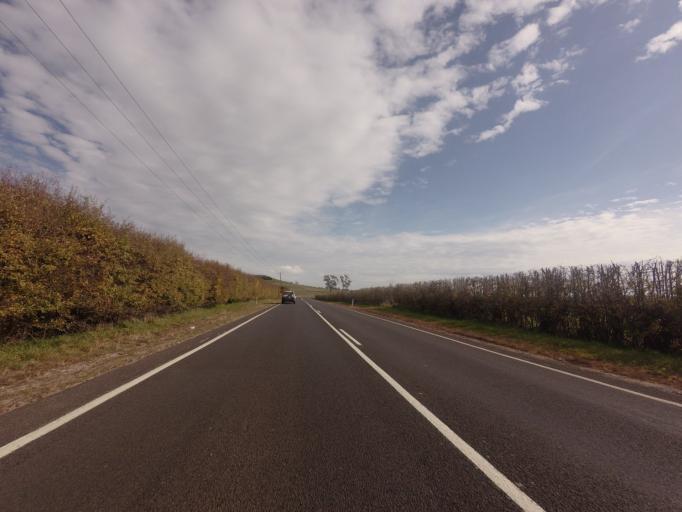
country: AU
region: Tasmania
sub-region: Meander Valley
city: Westbury
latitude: -41.5268
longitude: 146.7631
